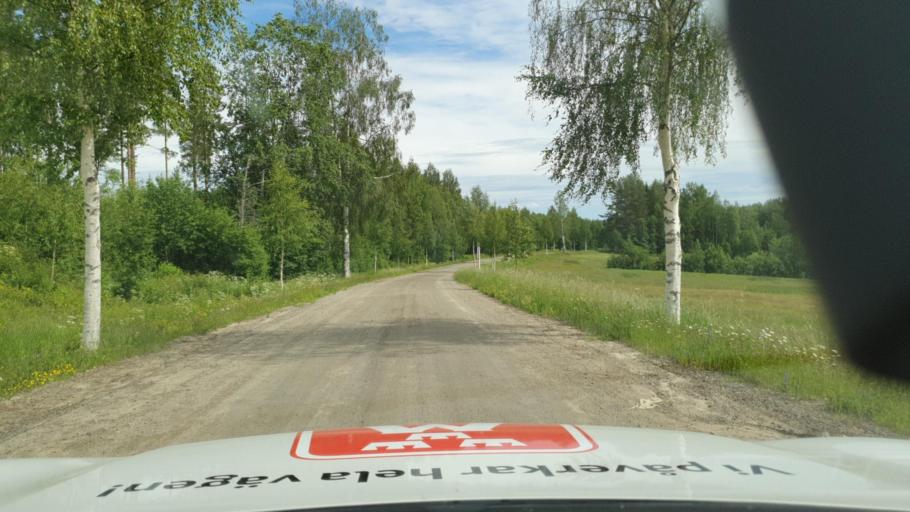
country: SE
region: Vaesterbotten
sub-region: Skelleftea Kommun
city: Burtraesk
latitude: 64.4796
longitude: 20.4332
